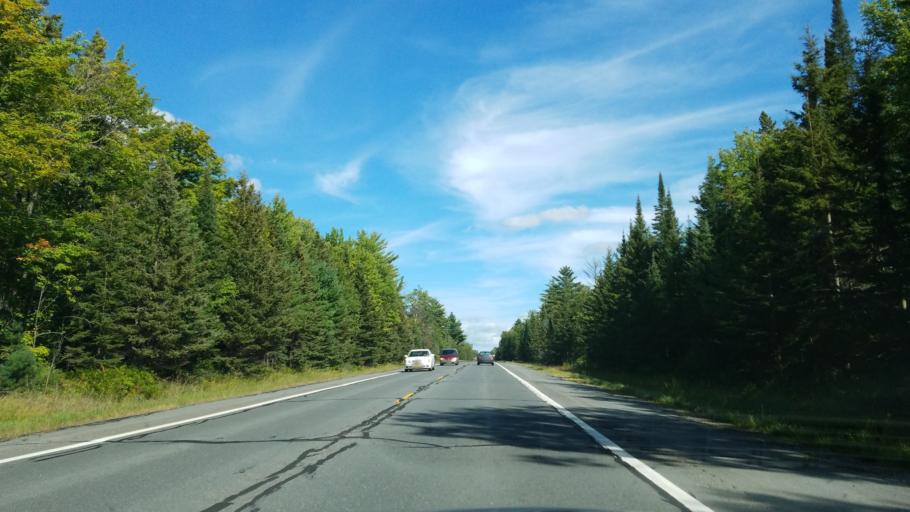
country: US
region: Michigan
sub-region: Baraga County
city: L'Anse
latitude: 46.5788
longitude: -88.4077
